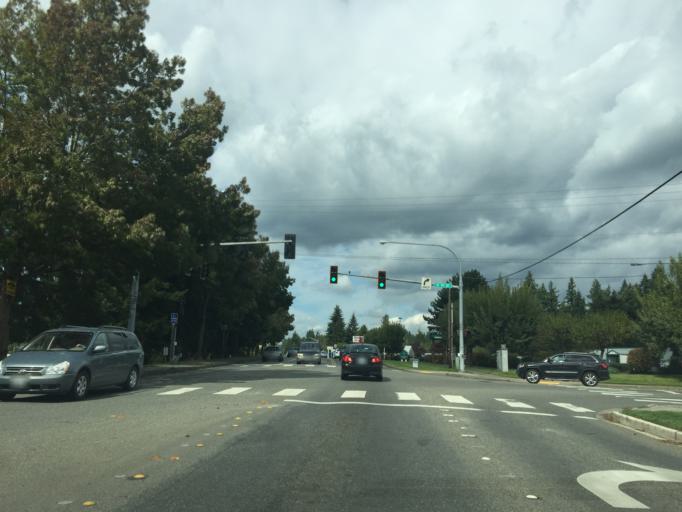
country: US
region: Washington
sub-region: Snohomish County
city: Snohomish
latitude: 47.9268
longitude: -122.0981
